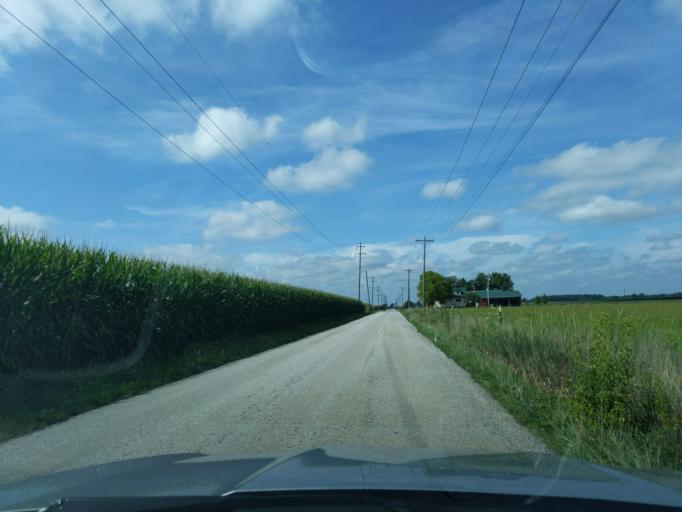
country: US
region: Indiana
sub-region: Ripley County
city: Batesville
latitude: 39.2629
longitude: -85.3474
